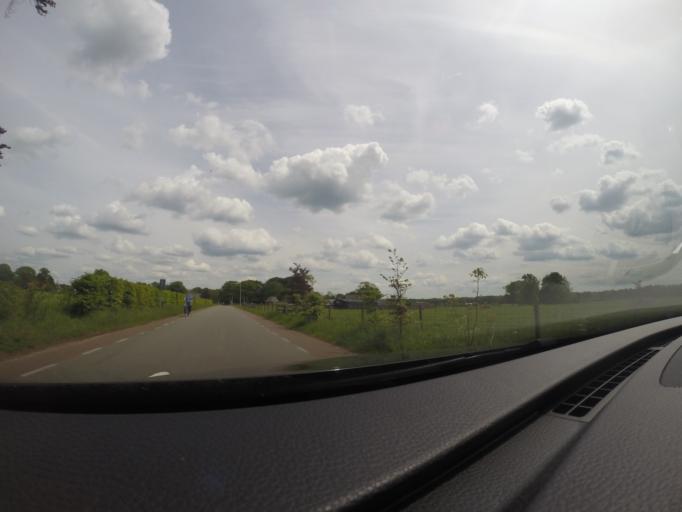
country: NL
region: Gelderland
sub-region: Gemeente Lochem
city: Almen
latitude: 52.1575
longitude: 6.3062
